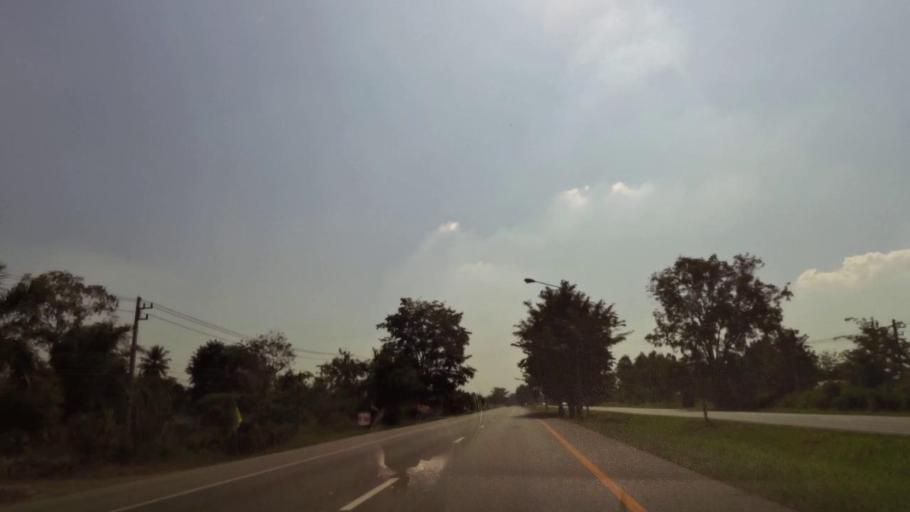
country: TH
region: Phichit
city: Bueng Na Rang
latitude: 16.2410
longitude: 100.1254
